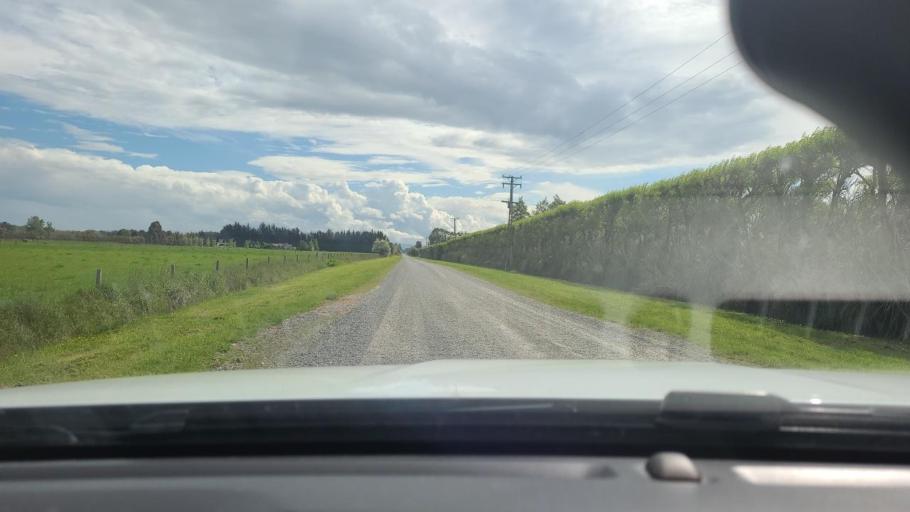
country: NZ
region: Southland
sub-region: Southland District
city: Winton
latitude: -46.1251
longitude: 168.3557
